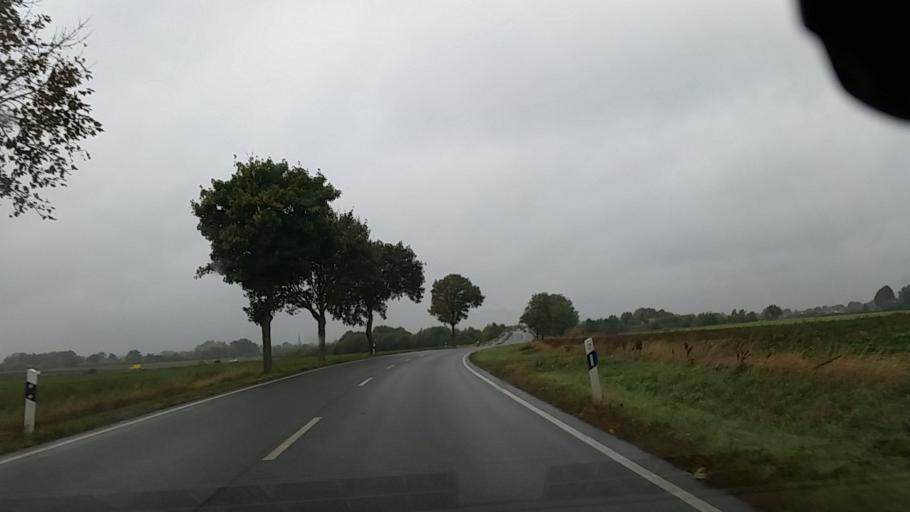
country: DE
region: Lower Saxony
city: Uelzen
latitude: 52.9452
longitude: 10.5885
